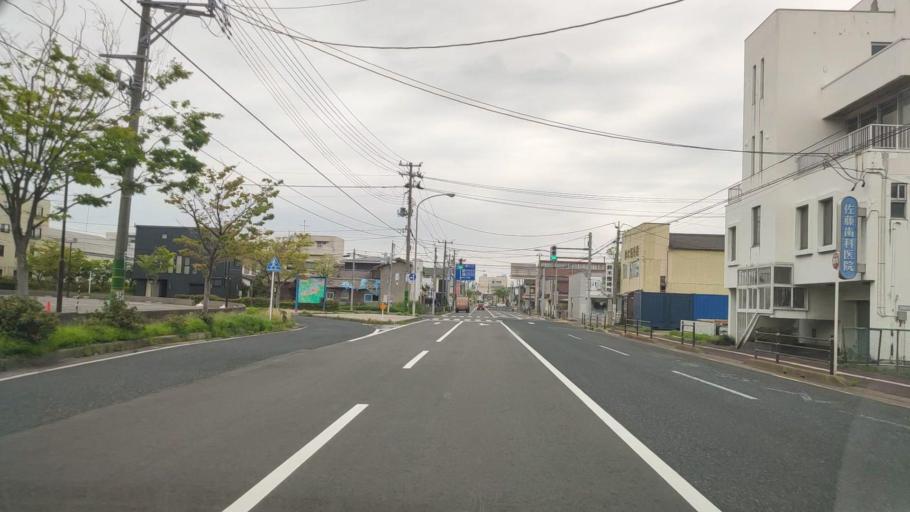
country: JP
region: Niigata
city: Niigata-shi
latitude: 37.9356
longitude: 139.0724
